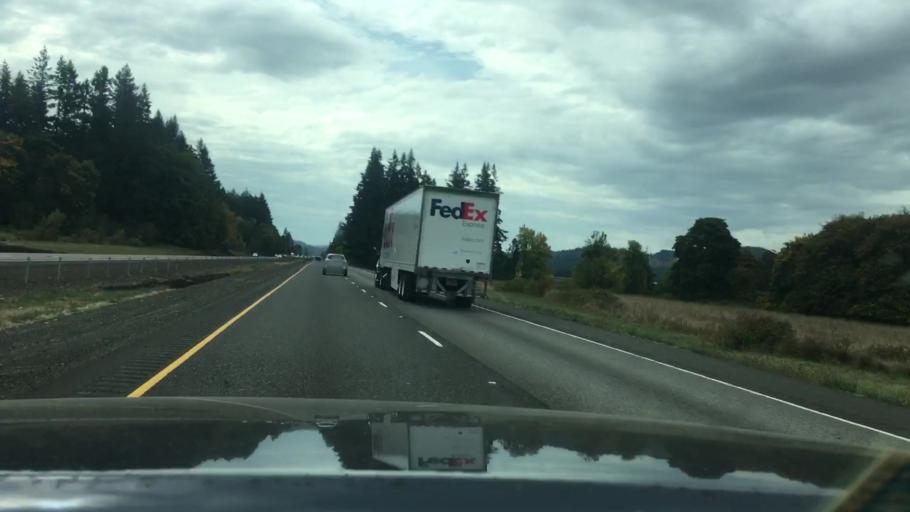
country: US
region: Oregon
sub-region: Lane County
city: Creswell
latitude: 43.8595
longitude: -123.0174
